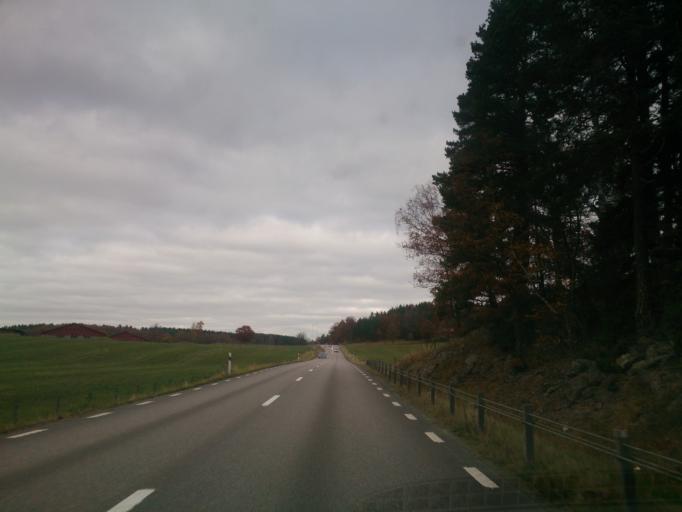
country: SE
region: OEstergoetland
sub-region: Atvidabergs Kommun
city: Atvidaberg
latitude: 58.2886
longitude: 15.8966
